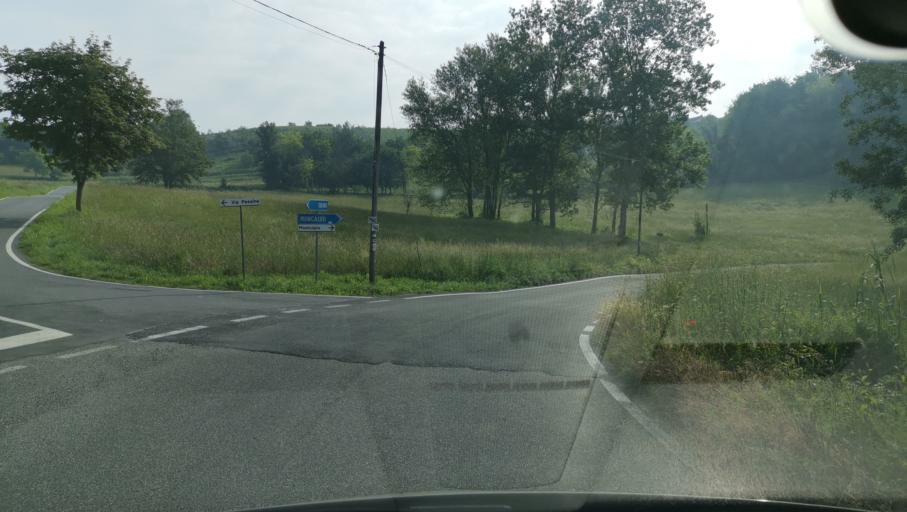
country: IT
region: Piedmont
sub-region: Provincia di Alessandria
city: Odalengo Piccolo
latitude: 45.0813
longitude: 8.1928
